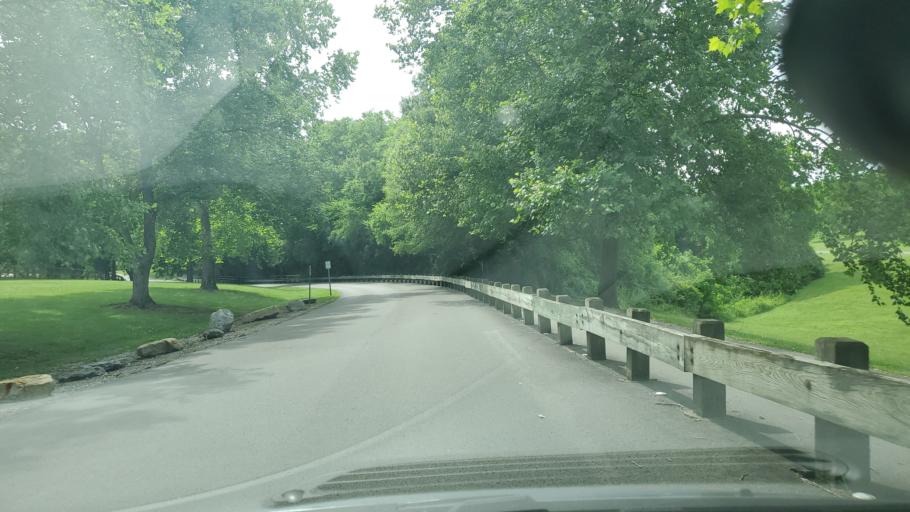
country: US
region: Tennessee
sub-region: Davidson County
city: Lakewood
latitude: 36.1923
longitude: -86.6747
